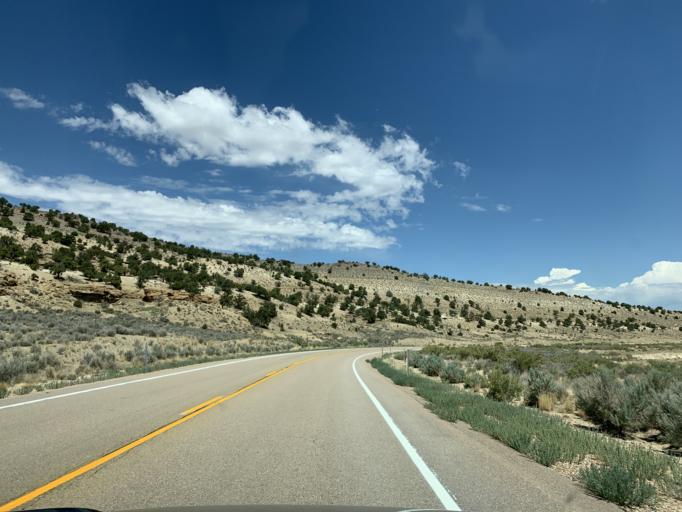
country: US
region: Utah
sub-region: Duchesne County
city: Duchesne
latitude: 39.9847
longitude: -110.1622
